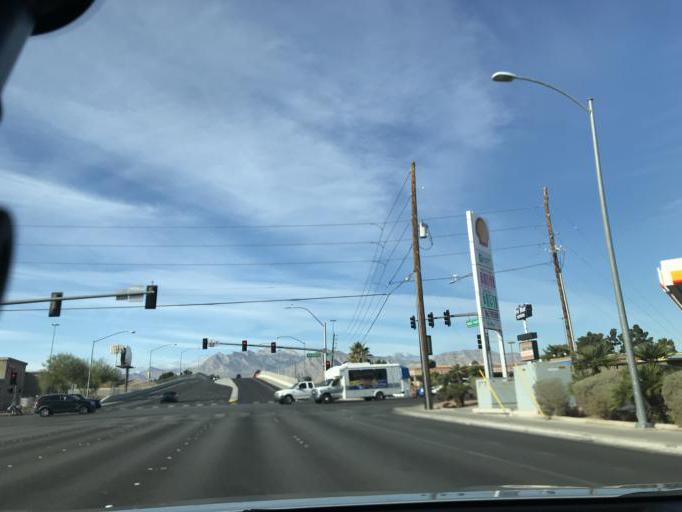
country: US
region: Nevada
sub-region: Clark County
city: Spring Valley
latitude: 36.2034
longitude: -115.2417
